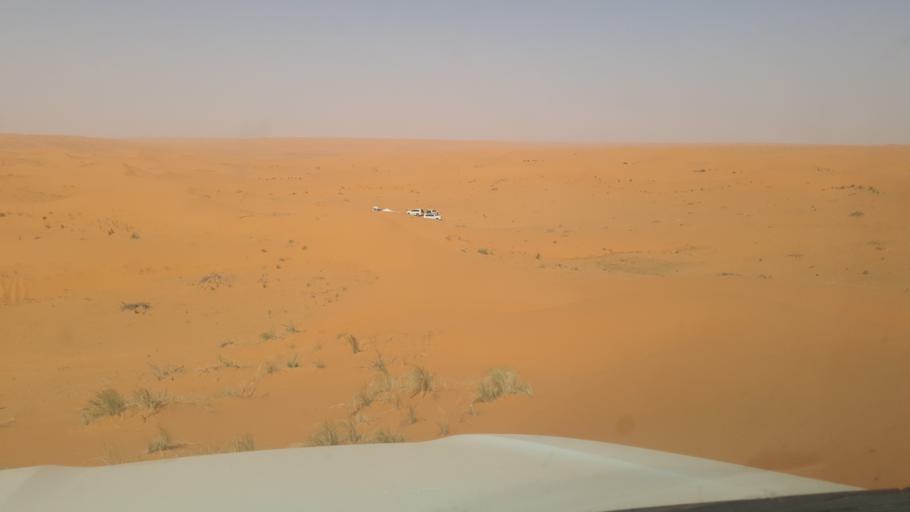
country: SA
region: Ar Riyad
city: Az Zulfi
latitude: 26.5790
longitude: 44.7977
